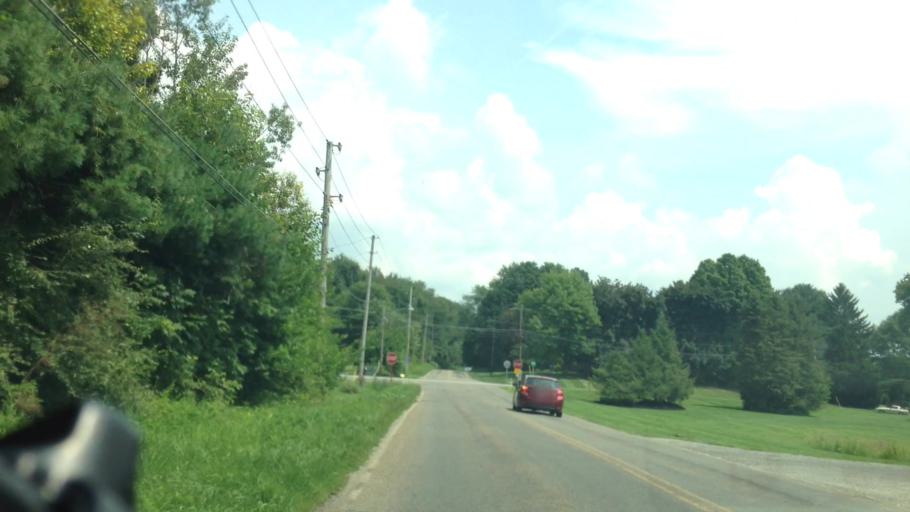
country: US
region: Ohio
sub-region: Stark County
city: Canal Fulton
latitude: 40.8633
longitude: -81.5690
